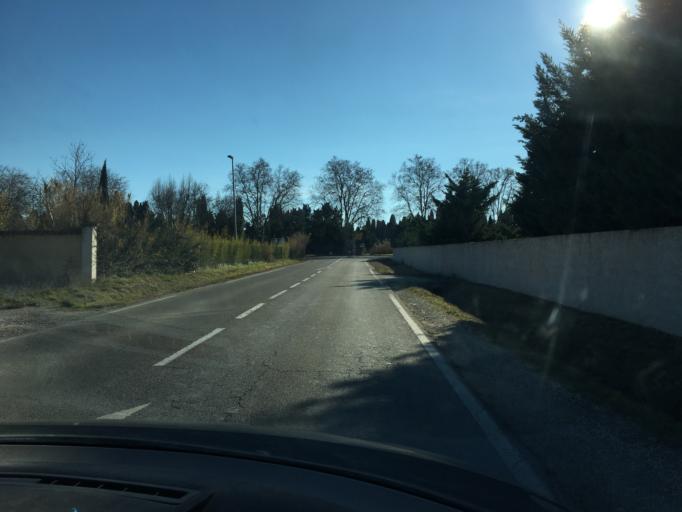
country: FR
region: Provence-Alpes-Cote d'Azur
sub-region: Departement des Bouches-du-Rhone
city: Maillane
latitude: 43.7969
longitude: 4.7889
